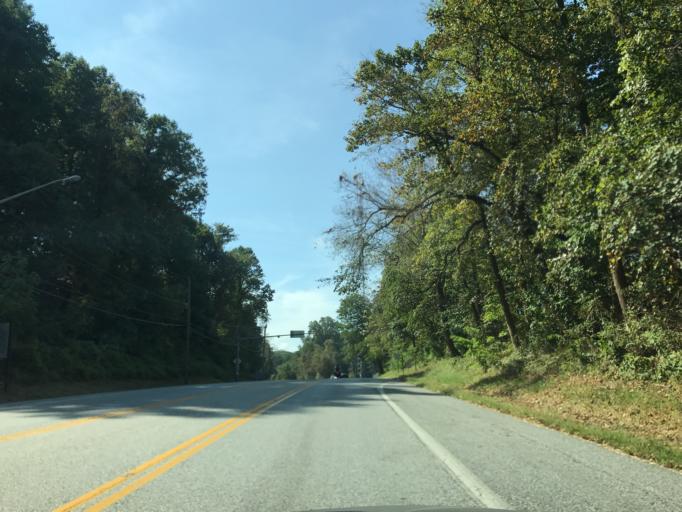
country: US
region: Maryland
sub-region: Cecil County
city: Rising Sun
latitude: 39.6551
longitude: -76.1781
